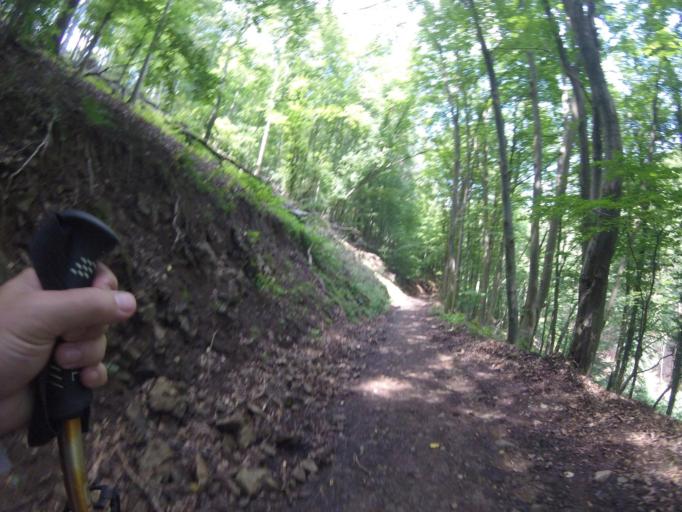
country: SK
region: Nitriansky
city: Sahy
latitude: 47.9585
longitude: 18.8959
